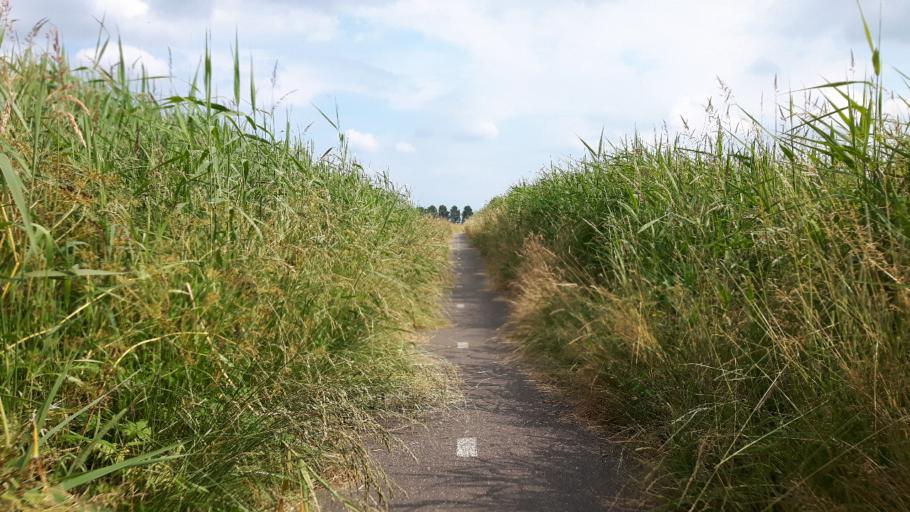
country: NL
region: Utrecht
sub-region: Stichtse Vecht
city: Spechtenkamp
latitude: 52.1224
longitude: 4.9700
